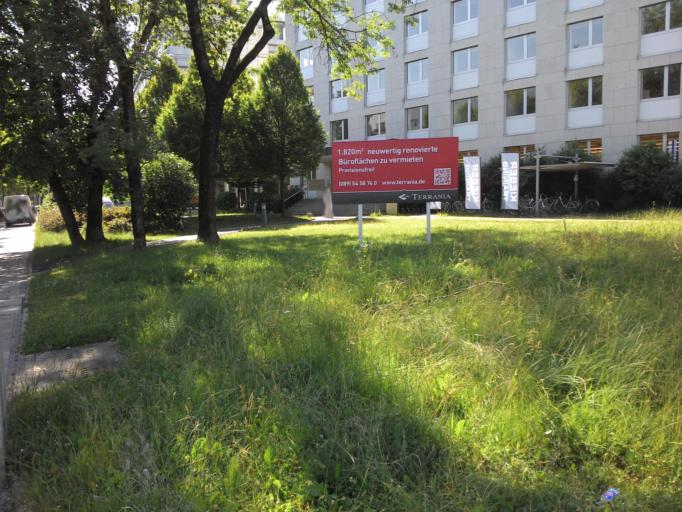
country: DE
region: Bavaria
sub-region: Upper Bavaria
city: Munich
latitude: 48.1499
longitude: 11.5204
